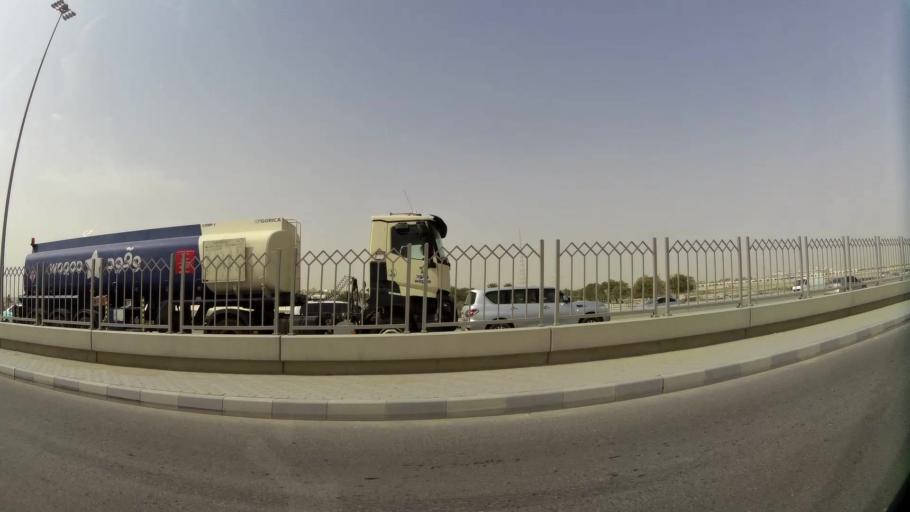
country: QA
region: Baladiyat ad Dawhah
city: Doha
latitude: 25.2866
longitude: 51.4818
